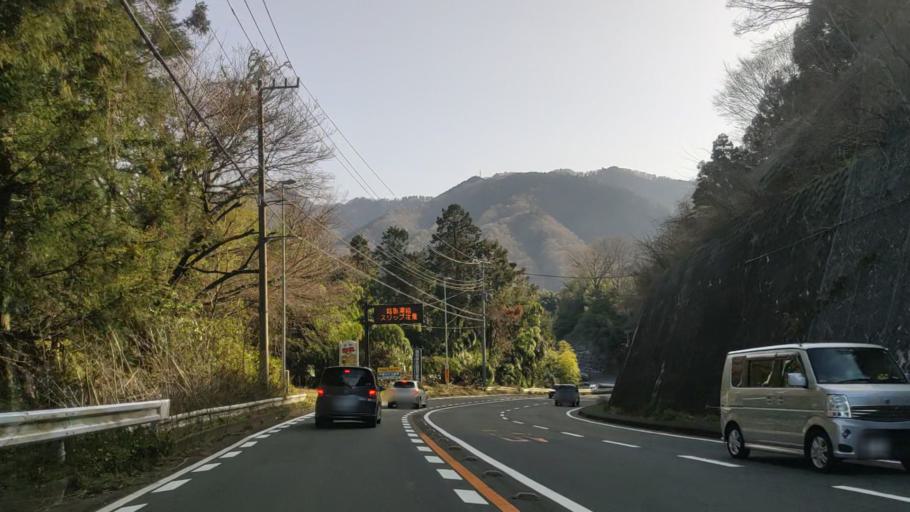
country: JP
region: Tokyo
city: Hachioji
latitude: 35.5474
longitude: 139.2631
